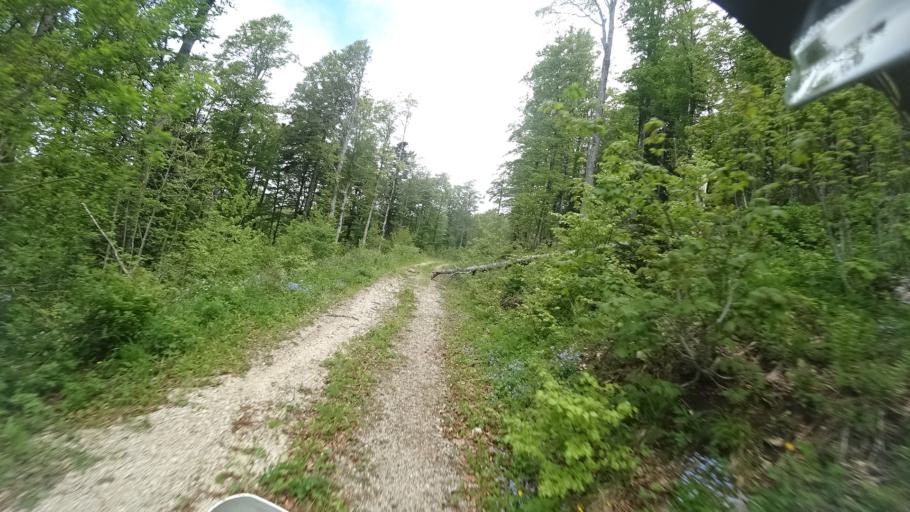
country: BA
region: Federation of Bosnia and Herzegovina
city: Orasac
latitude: 44.5698
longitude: 15.8692
